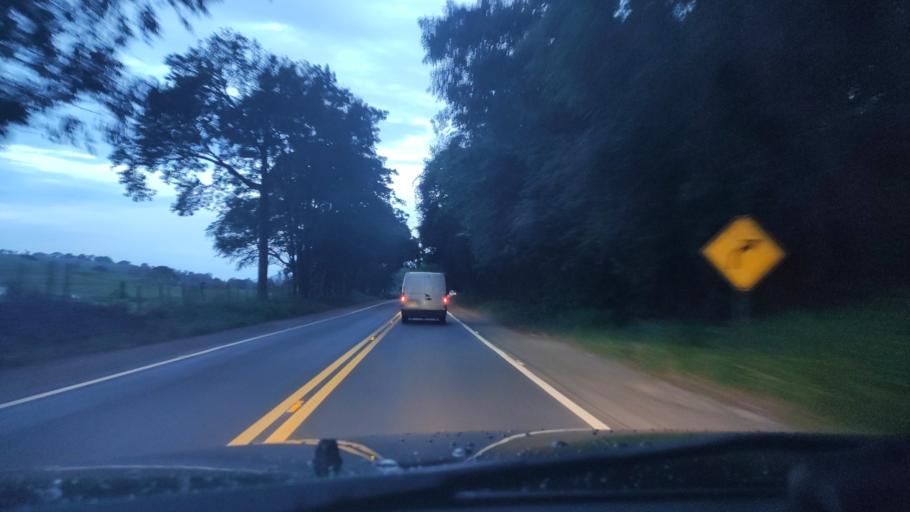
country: BR
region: Sao Paulo
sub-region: Socorro
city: Socorro
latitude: -22.6515
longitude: -46.5425
